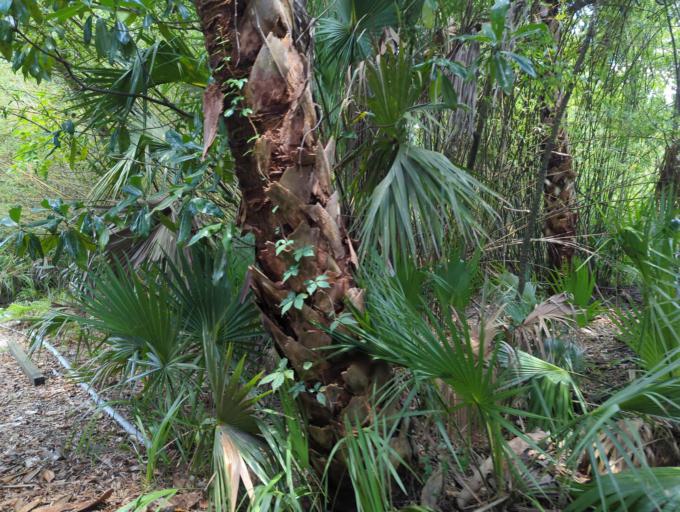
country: US
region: Florida
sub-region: Duval County
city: Jacksonville
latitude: 30.4053
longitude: -81.6444
